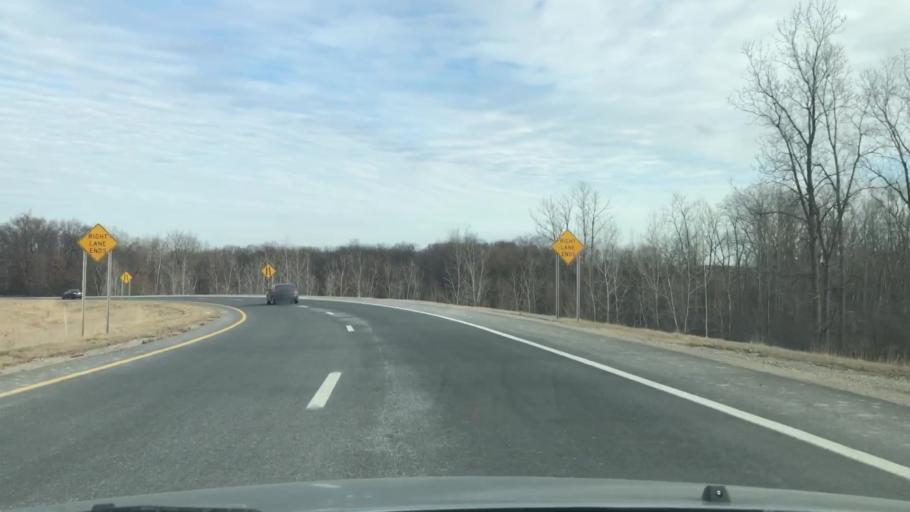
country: US
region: Michigan
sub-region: Oakland County
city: Auburn Hills
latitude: 42.6412
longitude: -83.2191
